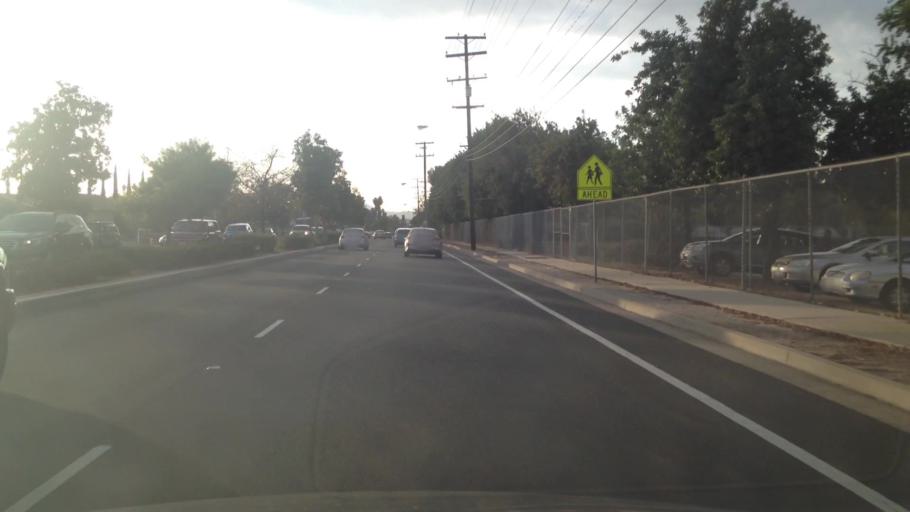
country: US
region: California
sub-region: Riverside County
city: Riverside
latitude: 33.9539
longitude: -117.3643
